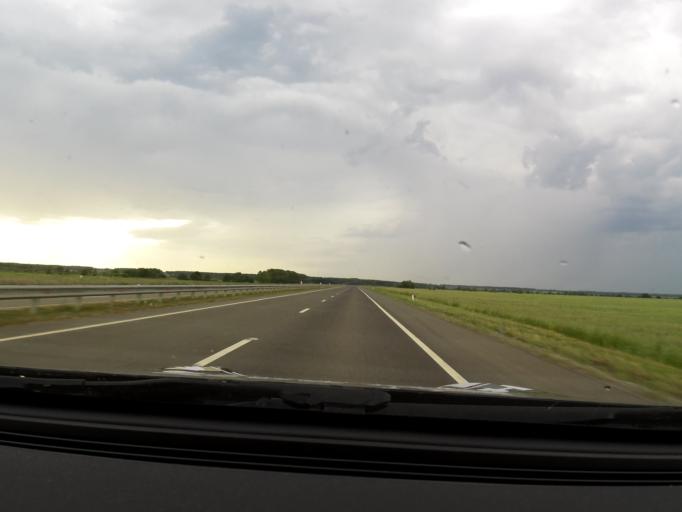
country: RU
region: Bashkortostan
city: Kushnarenkovo
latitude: 55.0609
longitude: 55.4013
